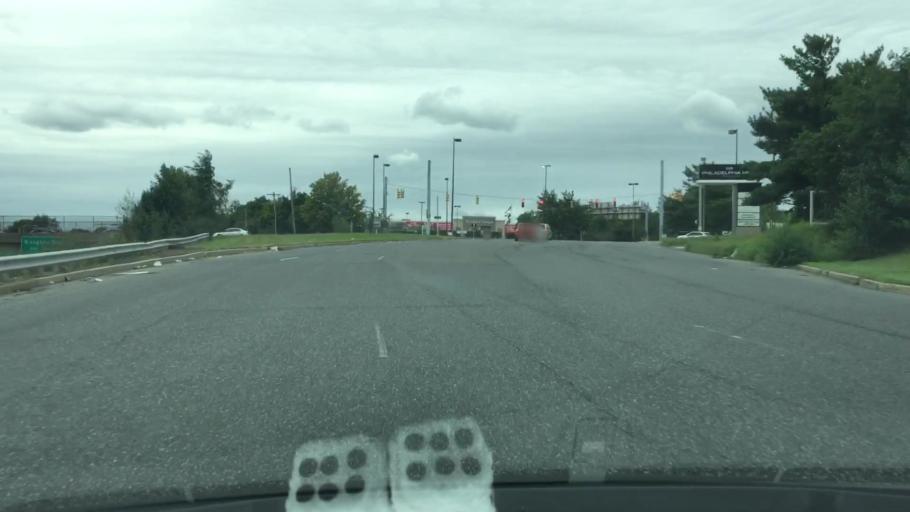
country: US
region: Pennsylvania
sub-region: Bucks County
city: Cornwells Heights
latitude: 40.0815
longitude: -74.9658
